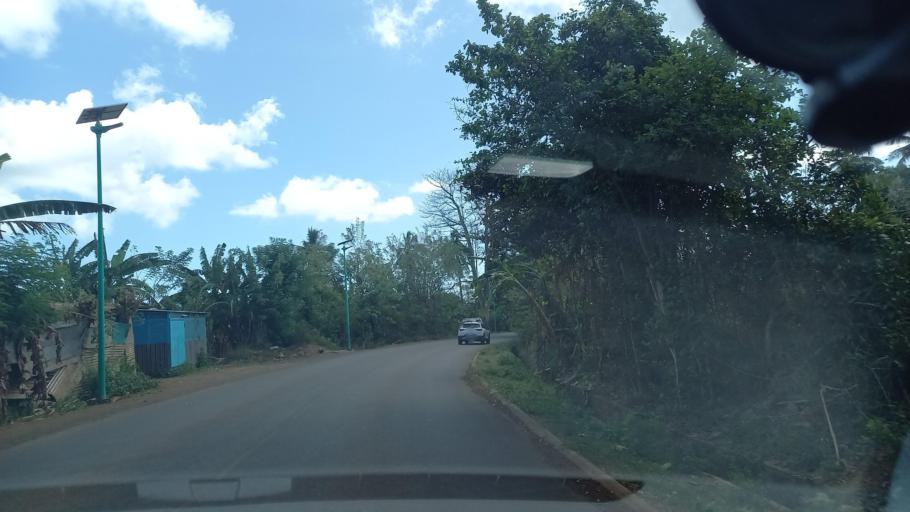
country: YT
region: Chirongui
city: Chirongui
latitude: -12.9070
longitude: 45.1538
